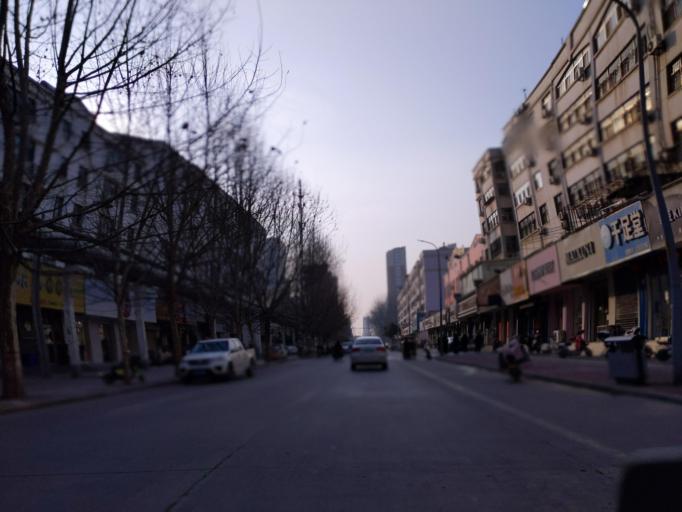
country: CN
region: Henan Sheng
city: Puyang
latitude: 35.7766
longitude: 115.0314
